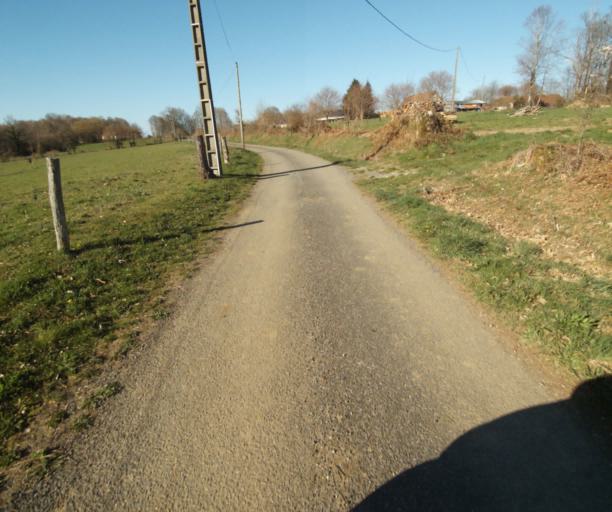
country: FR
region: Limousin
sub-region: Departement de la Correze
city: Seilhac
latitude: 45.3879
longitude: 1.7069
